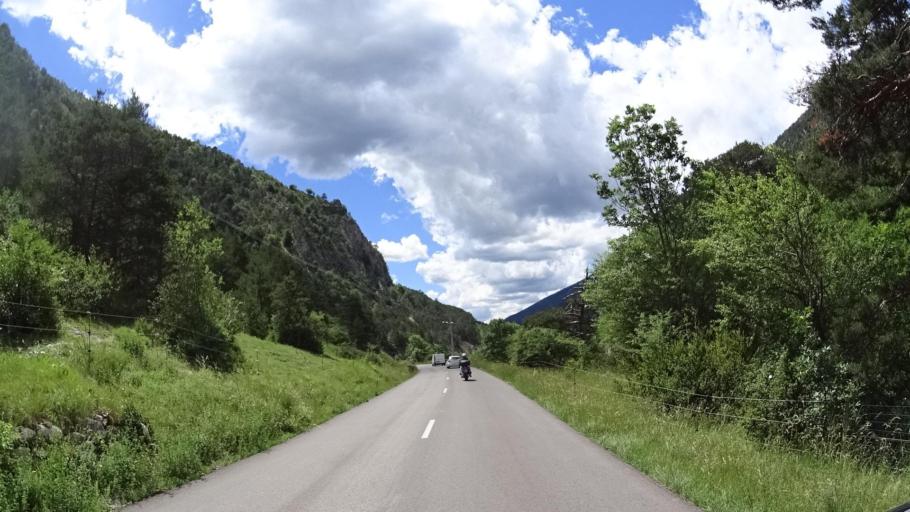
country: FR
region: Provence-Alpes-Cote d'Azur
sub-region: Departement des Alpes-de-Haute-Provence
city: Annot
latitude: 44.0559
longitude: 6.5734
